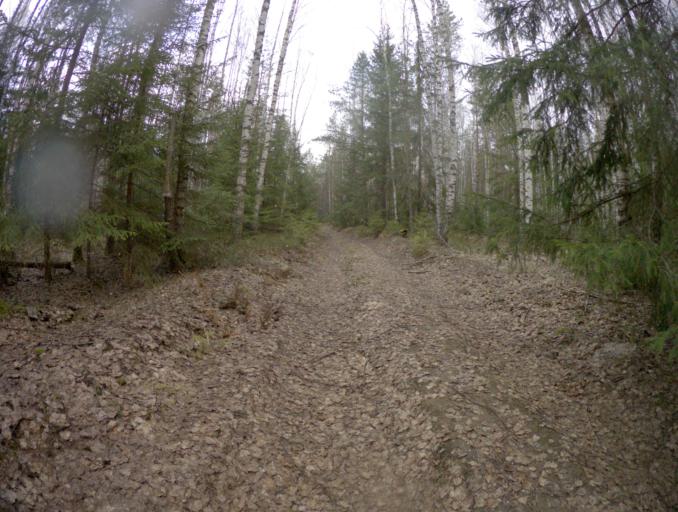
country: RU
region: Vladimir
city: Raduzhnyy
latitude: 55.9538
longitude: 40.2706
